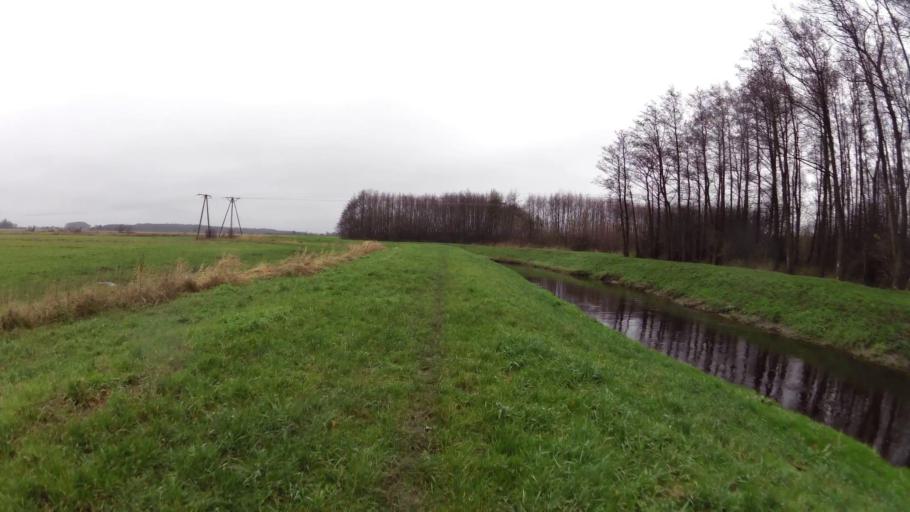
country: PL
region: West Pomeranian Voivodeship
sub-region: Koszalin
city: Koszalin
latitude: 54.2355
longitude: 16.1404
